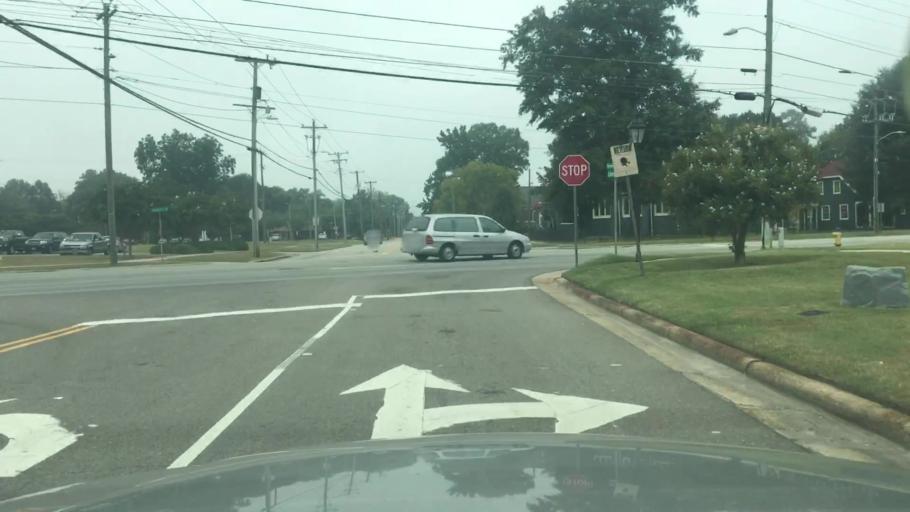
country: US
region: North Carolina
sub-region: Cumberland County
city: Fayetteville
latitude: 35.0596
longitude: -78.8769
